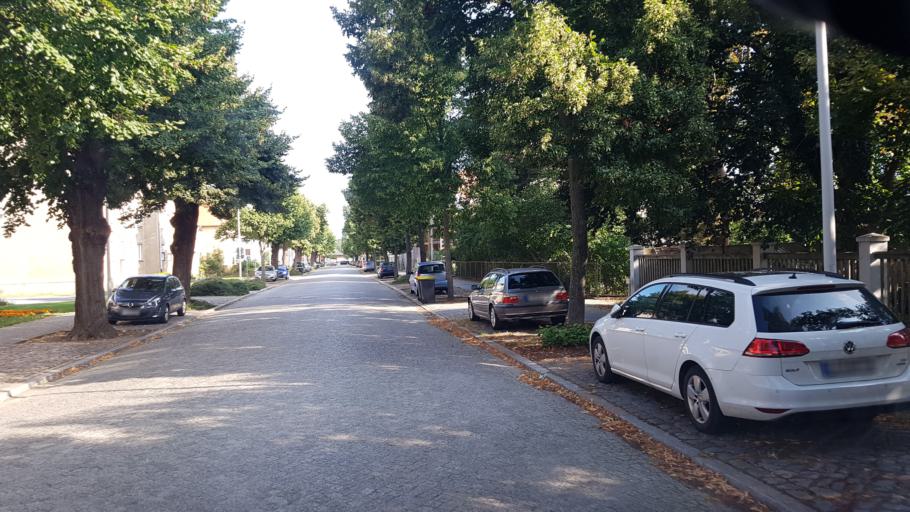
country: DE
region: Brandenburg
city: Luckau
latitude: 51.8547
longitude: 13.7144
